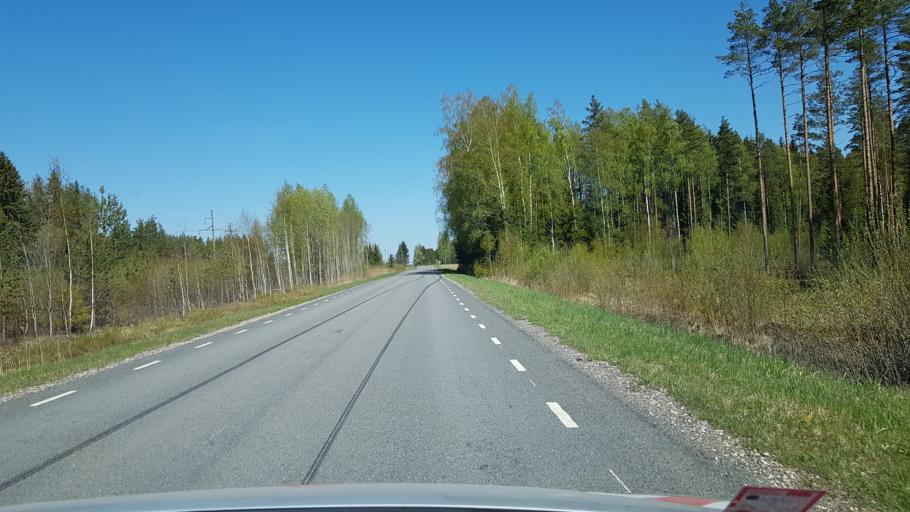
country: EE
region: Vorumaa
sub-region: Voru linn
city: Voru
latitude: 57.9380
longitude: 26.9528
